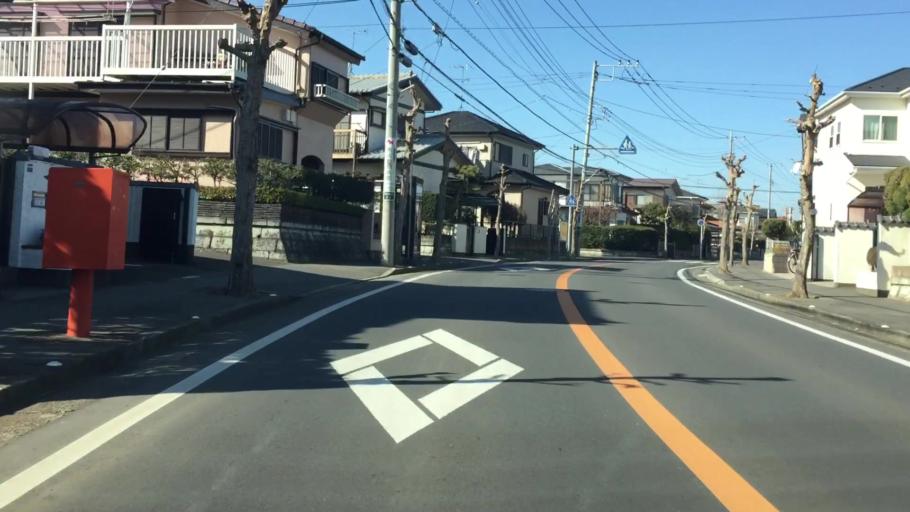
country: JP
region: Ibaraki
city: Fujishiro
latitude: 35.8528
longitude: 140.1290
